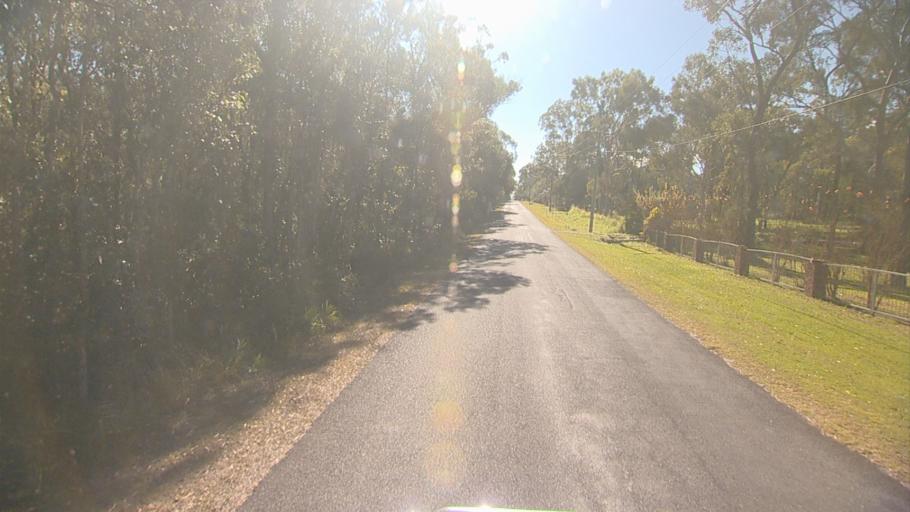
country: AU
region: Queensland
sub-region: Logan
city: Chambers Flat
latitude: -27.7433
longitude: 153.0940
